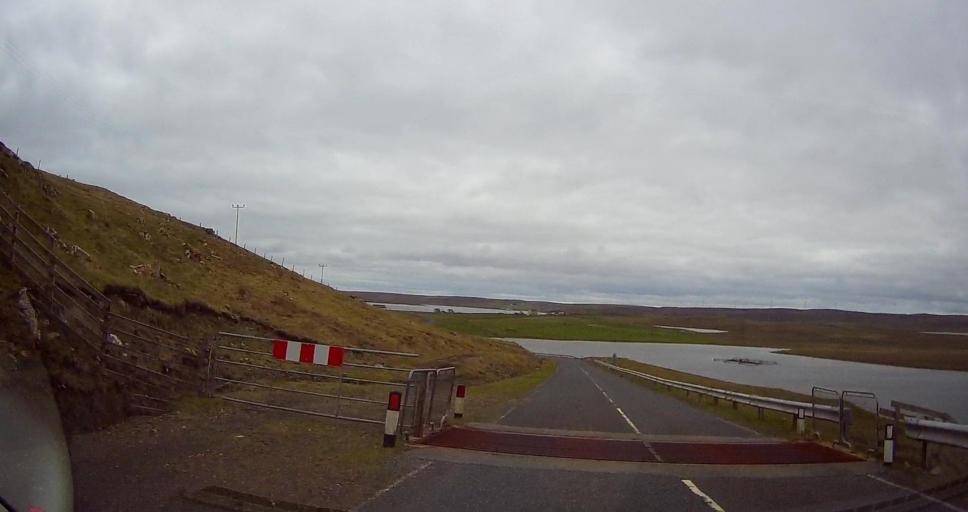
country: GB
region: Scotland
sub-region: Shetland Islands
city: Shetland
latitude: 60.6942
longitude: -0.9531
